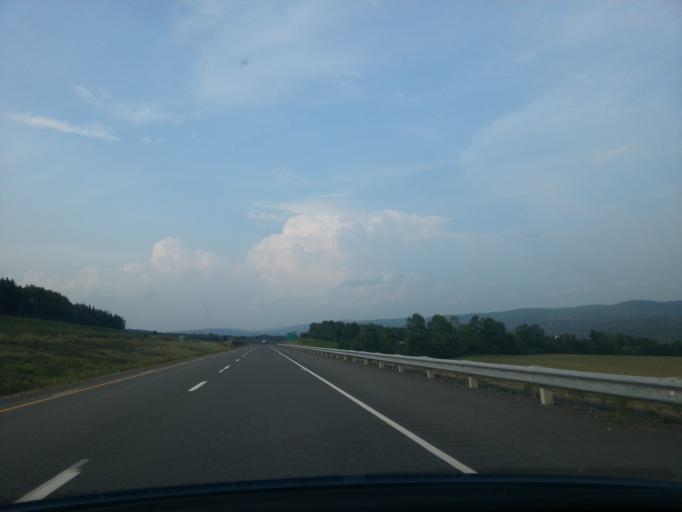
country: US
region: Maine
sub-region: Aroostook County
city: Fort Fairfield
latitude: 46.7195
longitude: -67.7312
